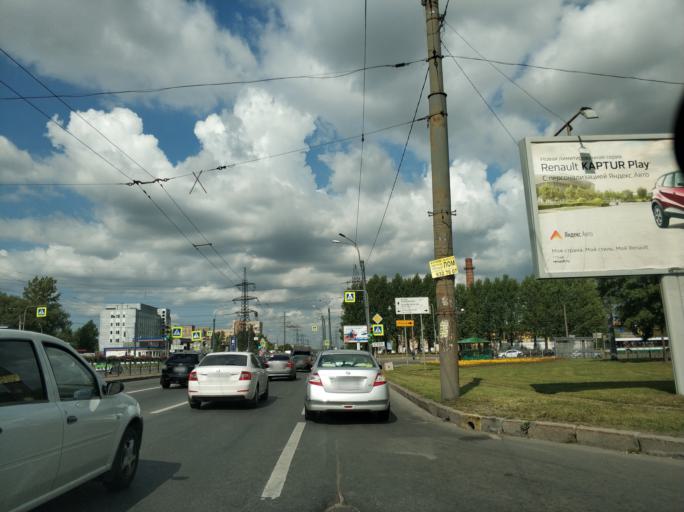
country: RU
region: St.-Petersburg
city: Krasnogvargeisky
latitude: 59.9553
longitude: 30.4678
